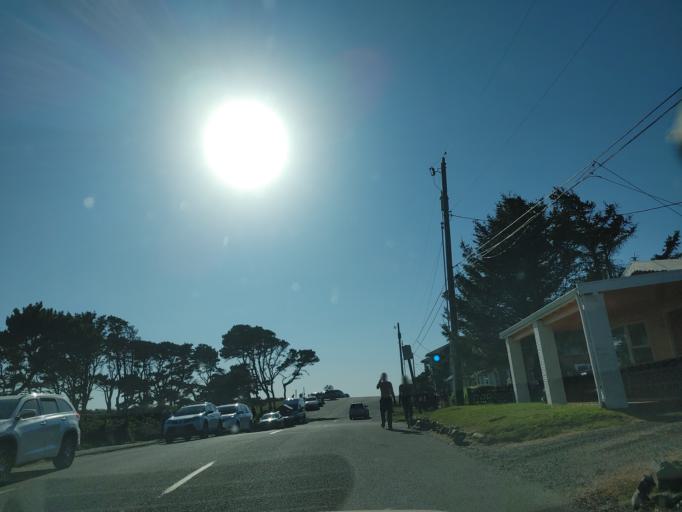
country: US
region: Oregon
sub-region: Lincoln County
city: Depoe Bay
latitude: 44.7472
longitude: -124.0630
